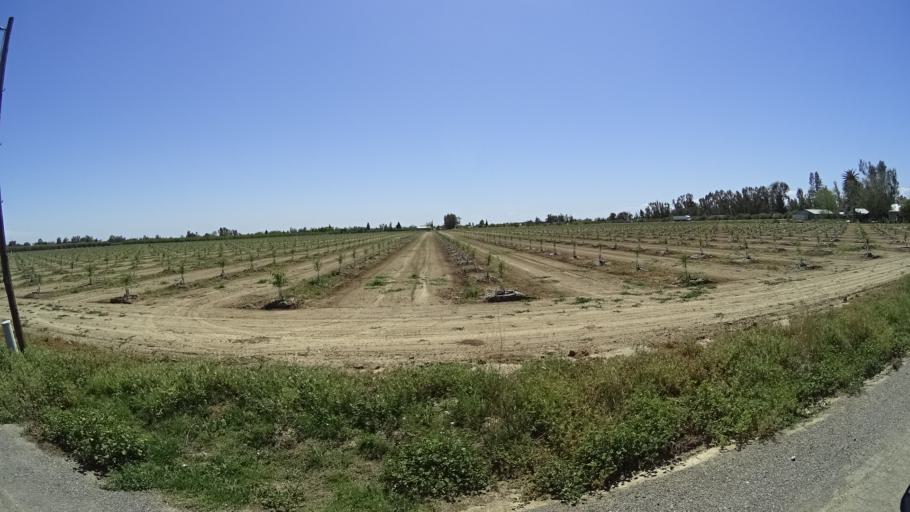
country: US
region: California
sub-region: Glenn County
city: Orland
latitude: 39.7334
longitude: -122.2033
